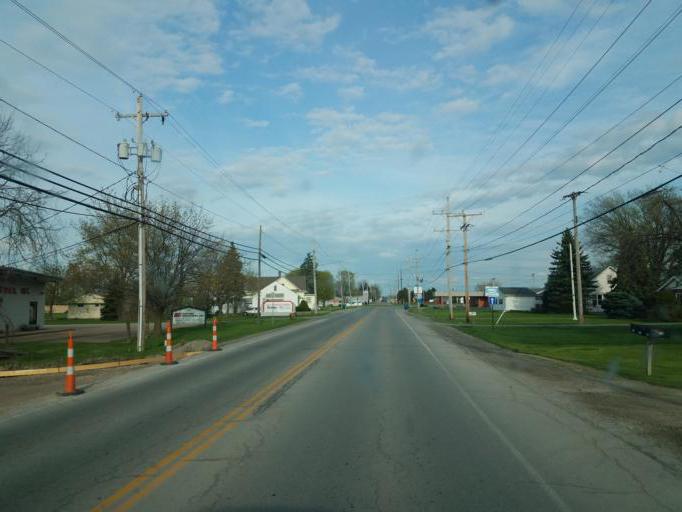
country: US
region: Ohio
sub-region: Erie County
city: Sandusky
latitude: 41.4414
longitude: -82.7495
